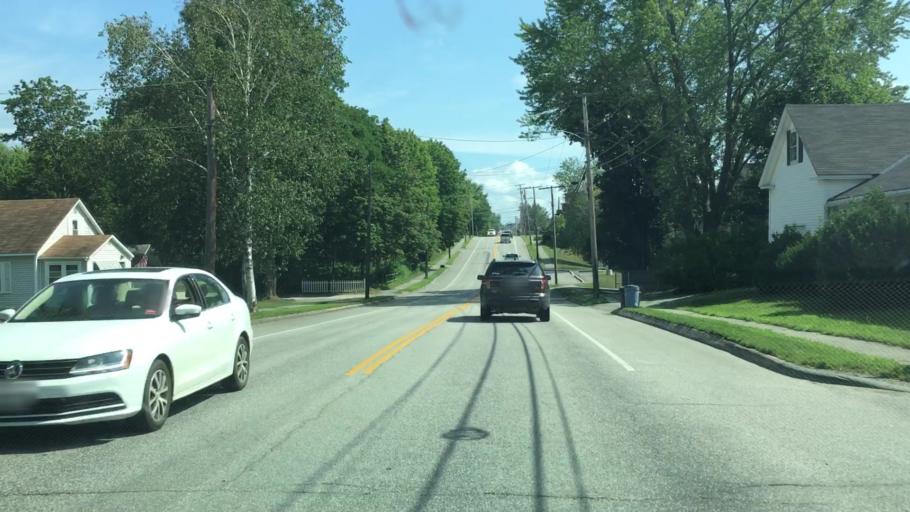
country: US
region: Maine
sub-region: Penobscot County
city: Brewer
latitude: 44.7928
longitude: -68.7583
